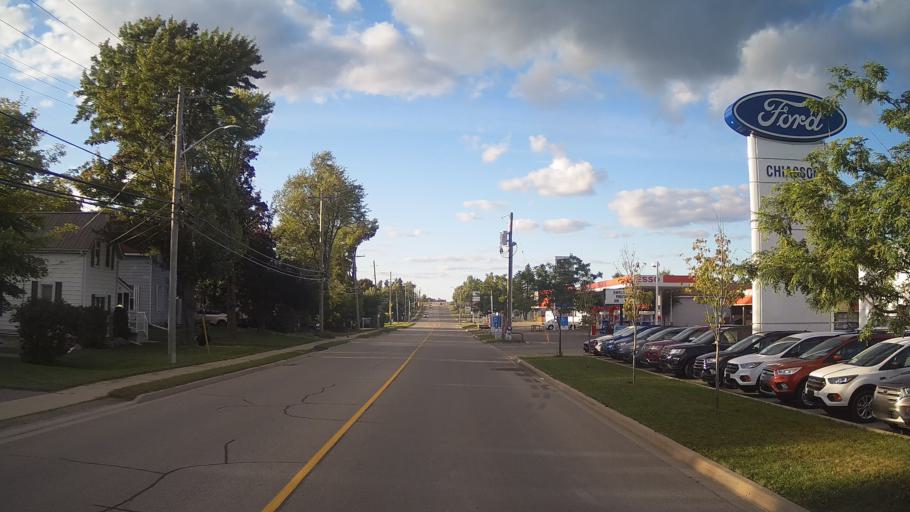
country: CA
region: Ontario
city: Gananoque
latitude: 44.3370
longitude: -76.1692
